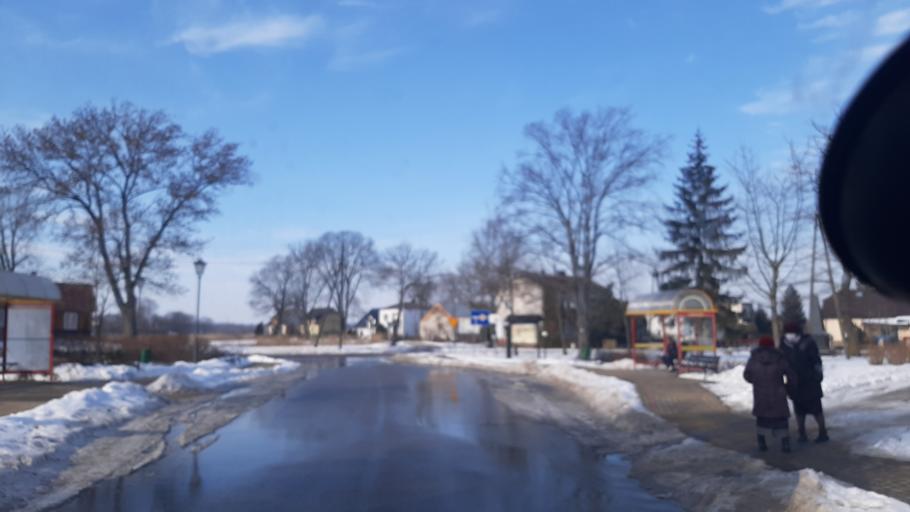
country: PL
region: Lublin Voivodeship
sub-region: Powiat pulawski
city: Baranow
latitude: 51.5582
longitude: 22.1361
